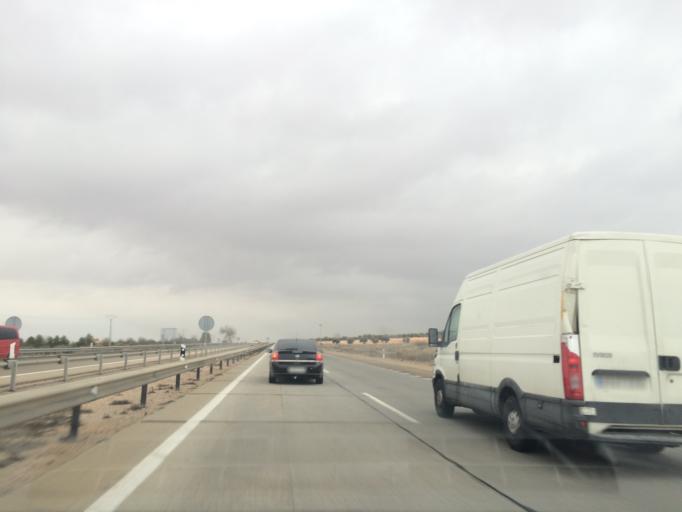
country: ES
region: Castille-La Mancha
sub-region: Province of Toledo
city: Madridejos
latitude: 39.5256
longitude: -3.5221
